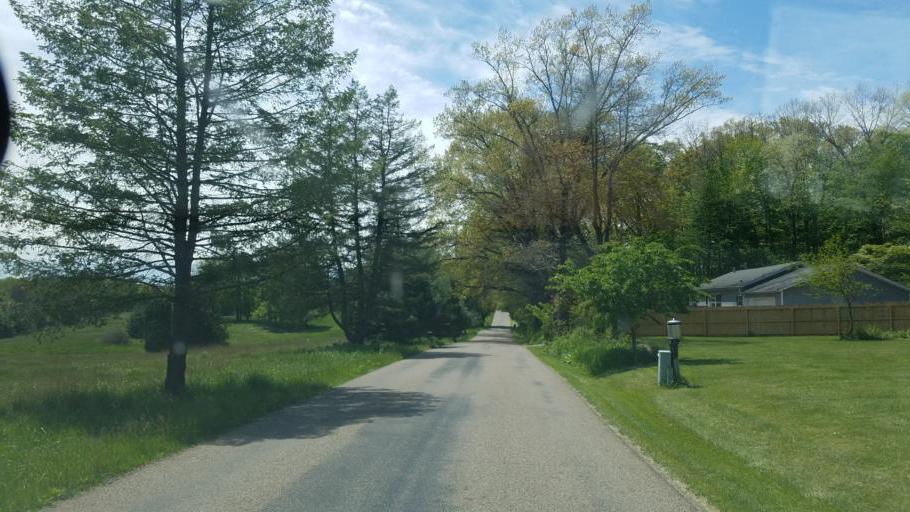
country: US
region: Ohio
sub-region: Knox County
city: Gambier
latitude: 40.3861
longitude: -82.3752
